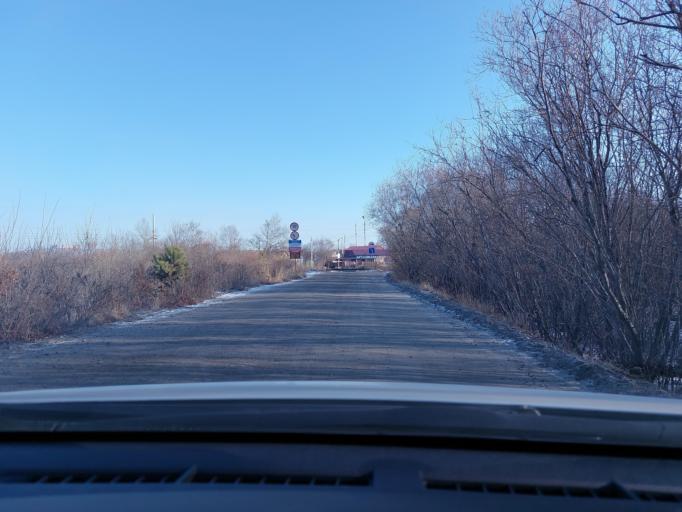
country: RU
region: Irkutsk
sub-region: Irkutskiy Rayon
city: Irkutsk
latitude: 52.3002
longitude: 104.2781
